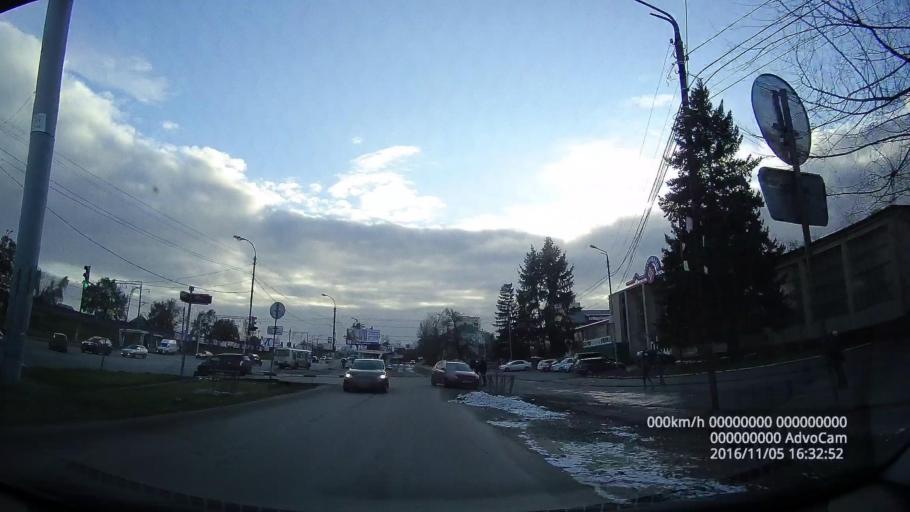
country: RU
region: Voronezj
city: Voronezh
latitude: 51.6837
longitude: 39.2159
